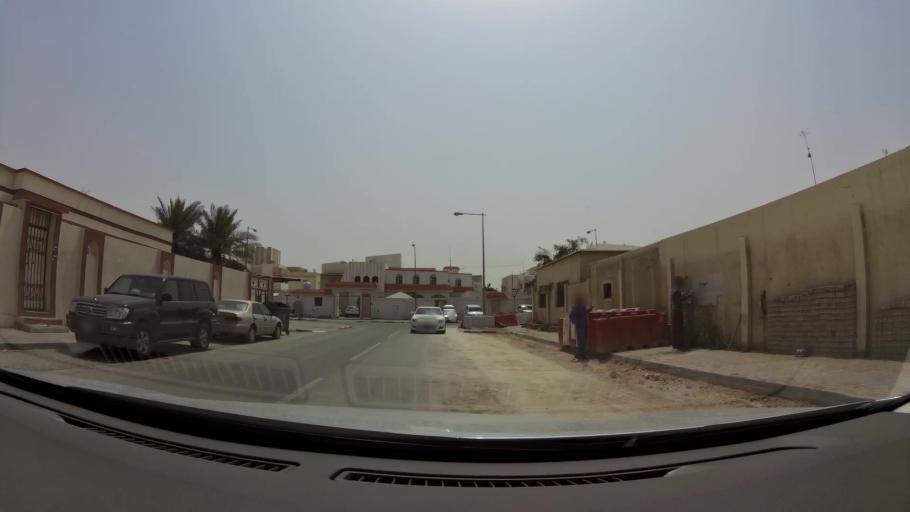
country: QA
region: Baladiyat ar Rayyan
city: Ar Rayyan
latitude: 25.2434
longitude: 51.4299
